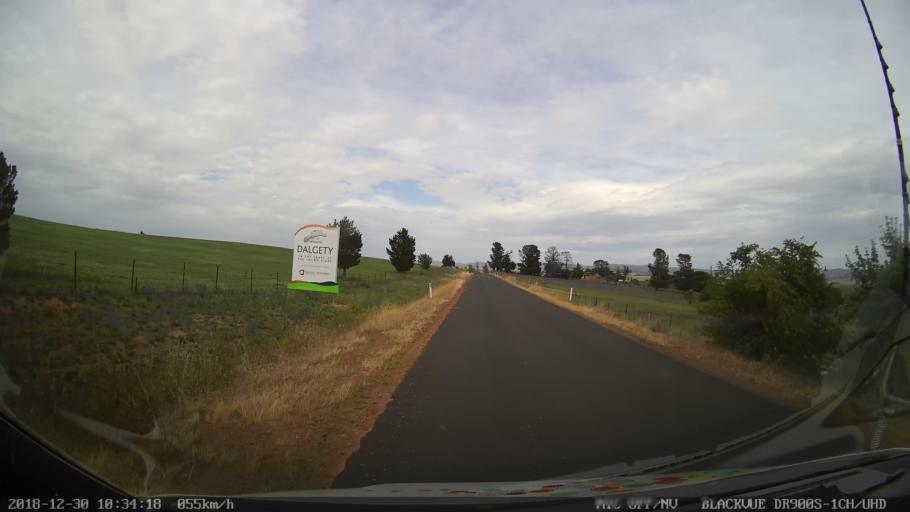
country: AU
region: New South Wales
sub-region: Snowy River
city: Berridale
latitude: -36.5004
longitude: 148.8419
